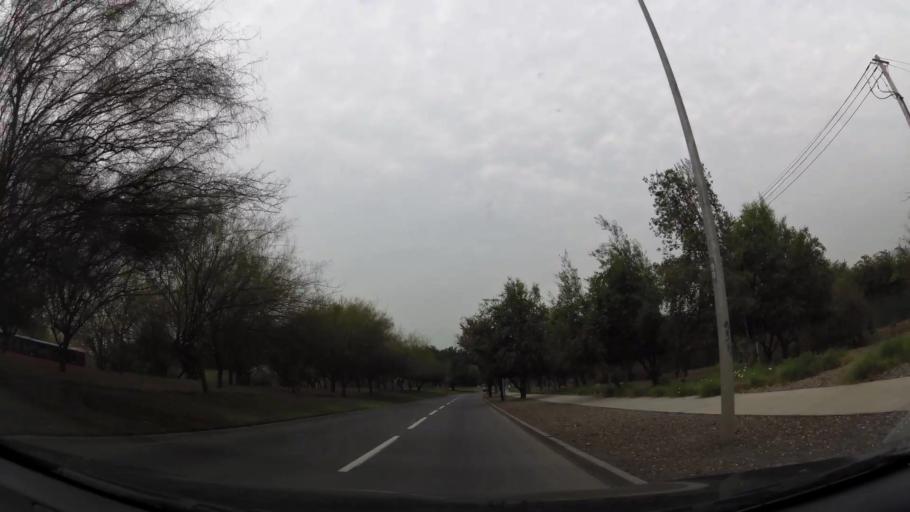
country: CL
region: Santiago Metropolitan
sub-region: Provincia de Chacabuco
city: Chicureo Abajo
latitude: -33.2818
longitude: -70.6391
